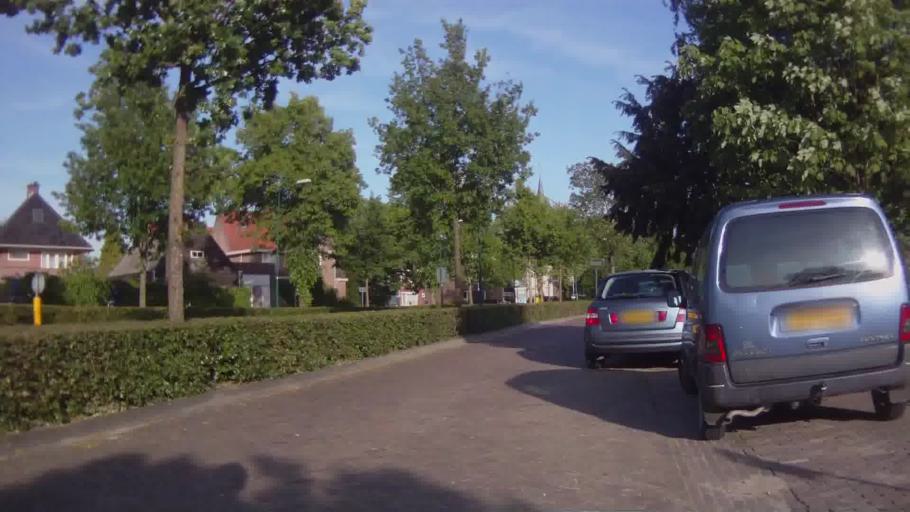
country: NL
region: Utrecht
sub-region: Gemeente Bunnik
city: Bunnik
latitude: 52.0669
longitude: 5.2015
